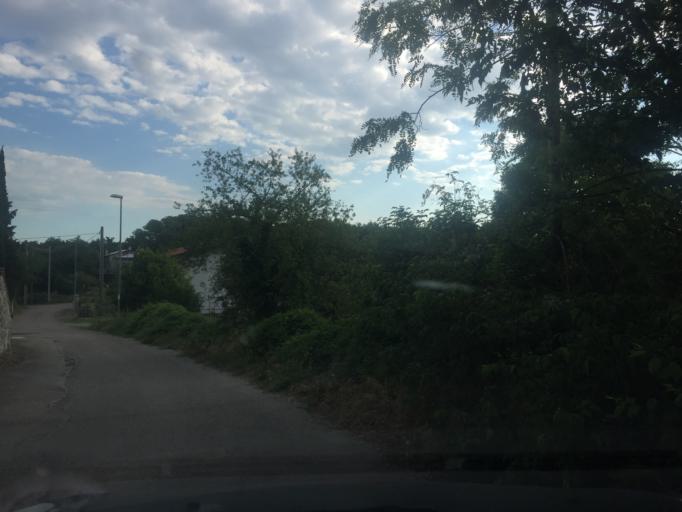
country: IT
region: Friuli Venezia Giulia
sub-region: Provincia di Gorizia
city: Savogna d'Isonzo
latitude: 45.8818
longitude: 13.5643
